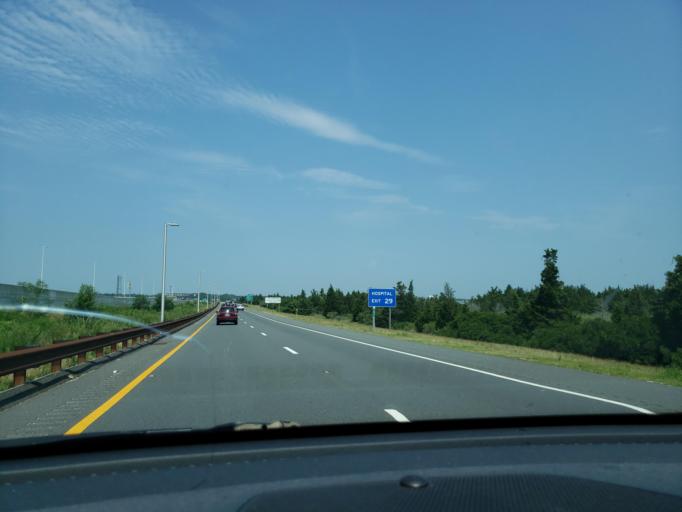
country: US
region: New Jersey
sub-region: Atlantic County
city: Somers Point
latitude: 39.2982
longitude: -74.6202
